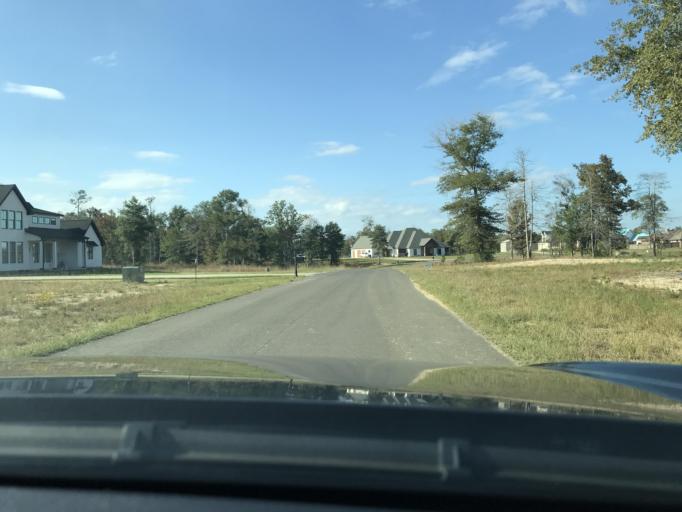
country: US
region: Louisiana
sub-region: Calcasieu Parish
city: Moss Bluff
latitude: 30.3330
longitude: -93.2509
